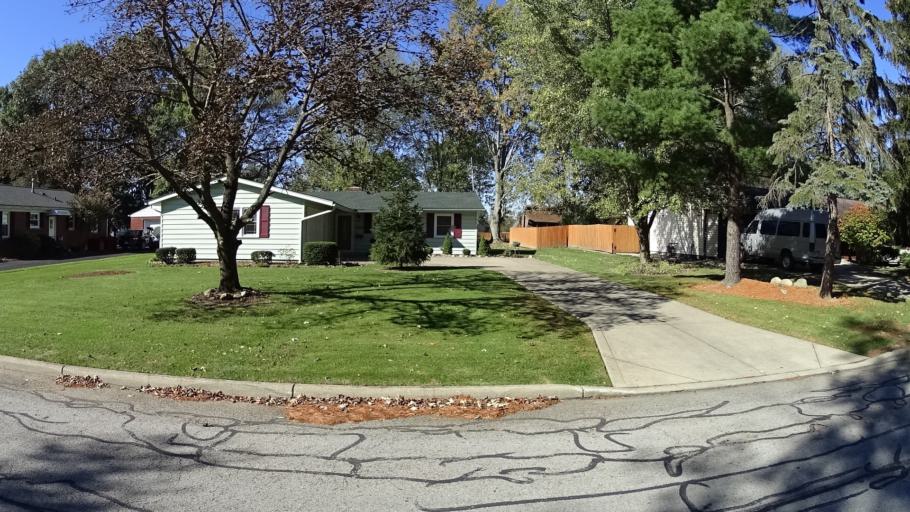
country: US
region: Ohio
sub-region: Lorain County
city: Oberlin
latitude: 41.2930
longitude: -82.1955
